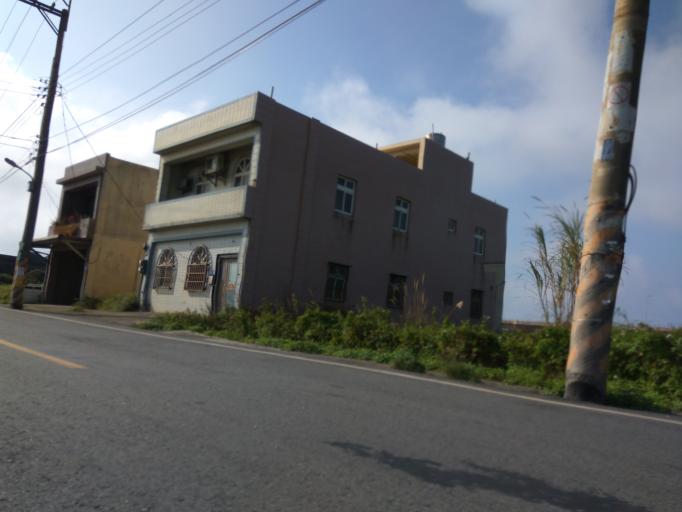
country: TW
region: Taiwan
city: Taoyuan City
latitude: 25.0789
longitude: 121.1720
